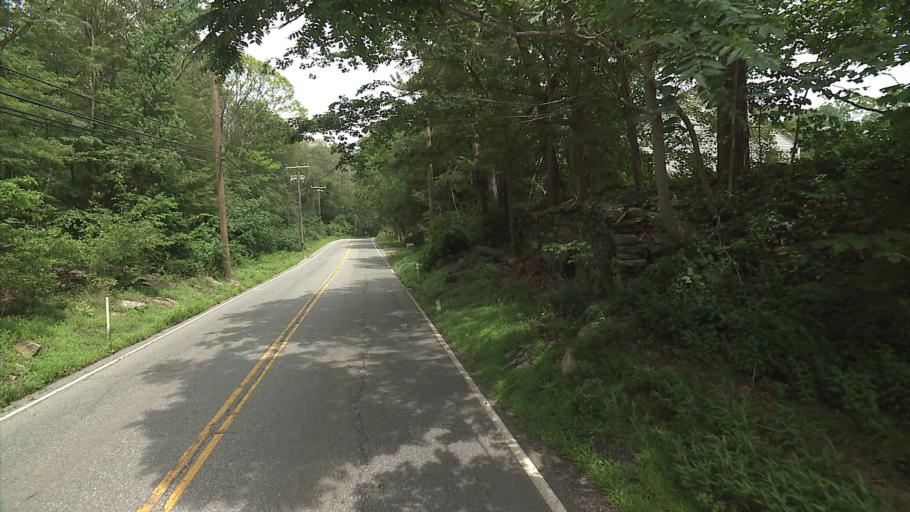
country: US
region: Connecticut
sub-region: Middlesex County
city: Deep River Center
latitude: 41.3644
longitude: -72.4675
